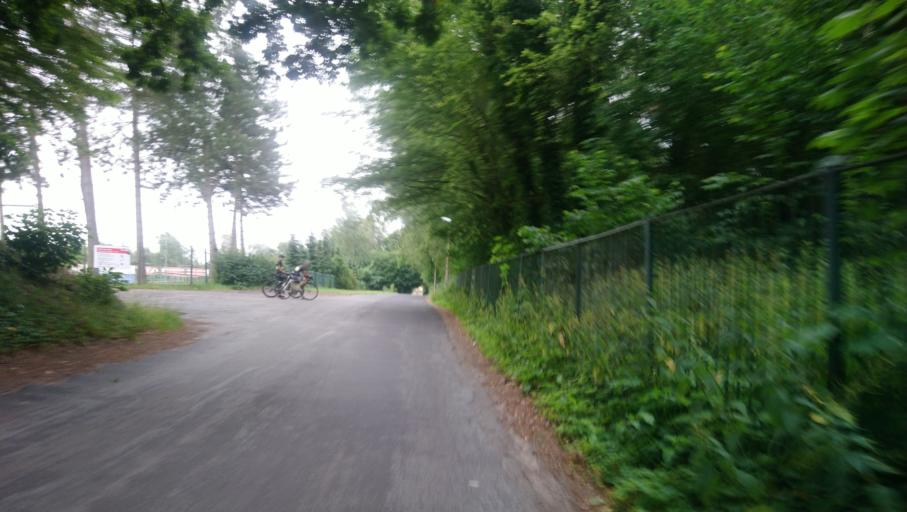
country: DE
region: Mecklenburg-Vorpommern
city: Kritzmow
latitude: 54.0693
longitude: 12.0966
